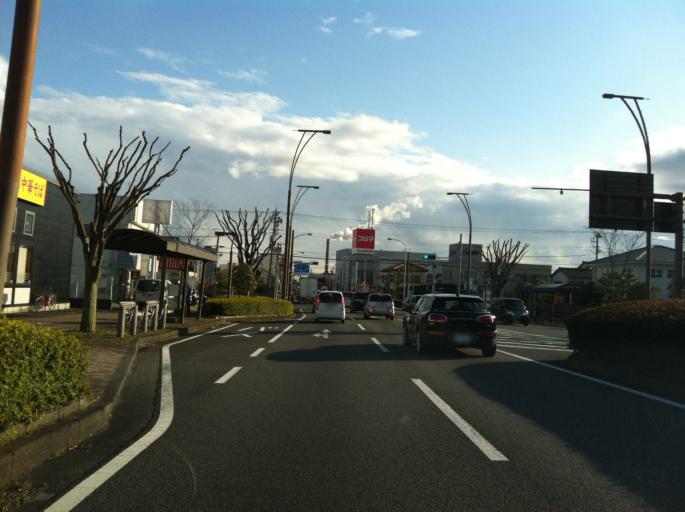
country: JP
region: Shizuoka
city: Fuji
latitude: 35.1577
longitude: 138.6658
